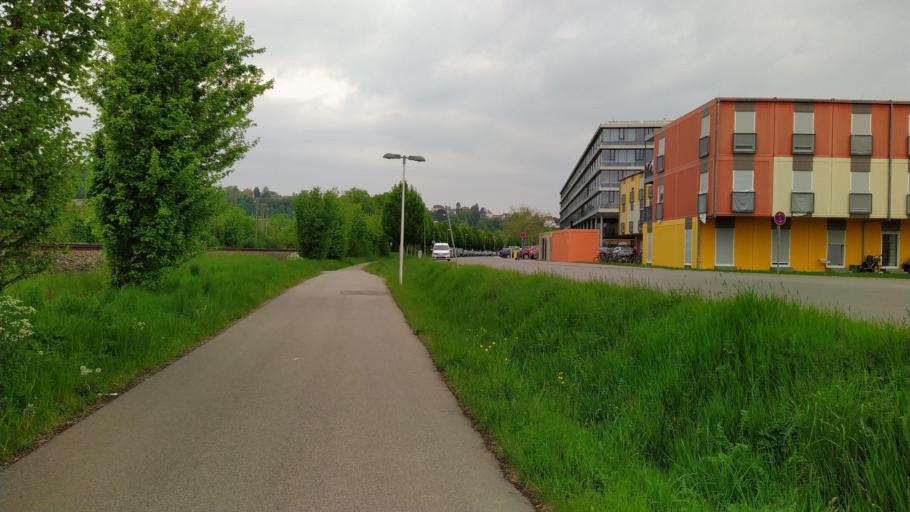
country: DE
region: Baden-Wuerttemberg
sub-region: Tuebingen Region
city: Tuebingen
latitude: 48.5093
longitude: 9.0465
